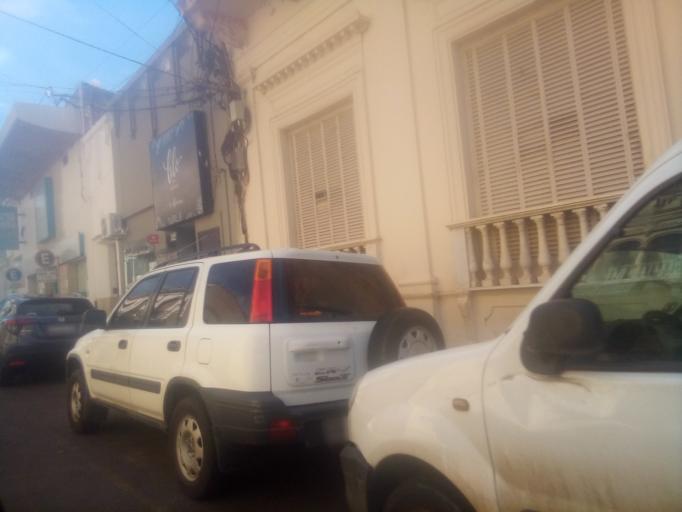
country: AR
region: Corrientes
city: Corrientes
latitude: -27.4646
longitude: -58.8365
